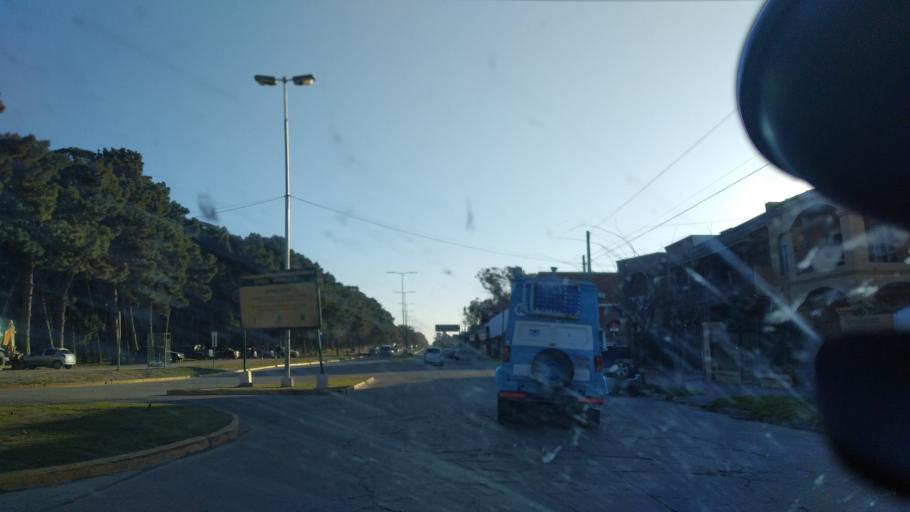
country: AR
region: Buenos Aires
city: Necochea
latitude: -38.5820
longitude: -58.7415
